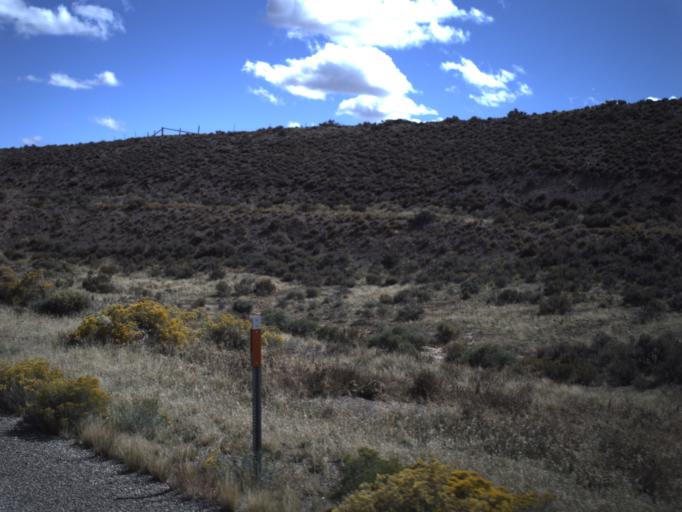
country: US
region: Utah
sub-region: Beaver County
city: Milford
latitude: 38.4387
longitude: -113.1516
